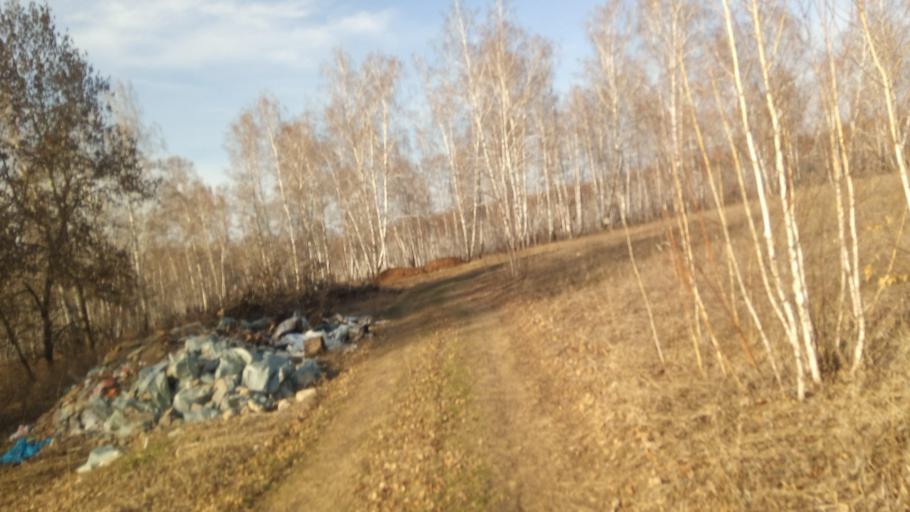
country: RU
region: Chelyabinsk
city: Sargazy
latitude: 55.1147
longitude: 61.2382
